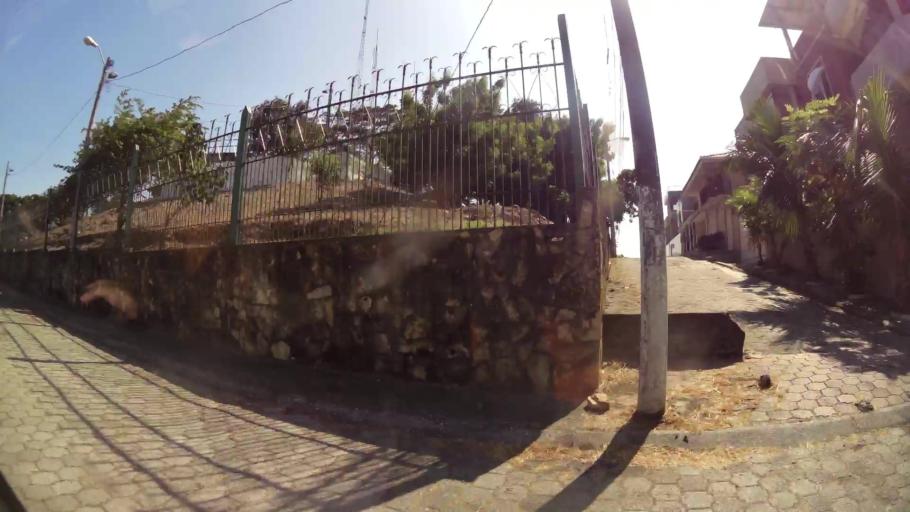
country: EC
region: Guayas
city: Guayaquil
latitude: -2.1834
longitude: -79.9145
